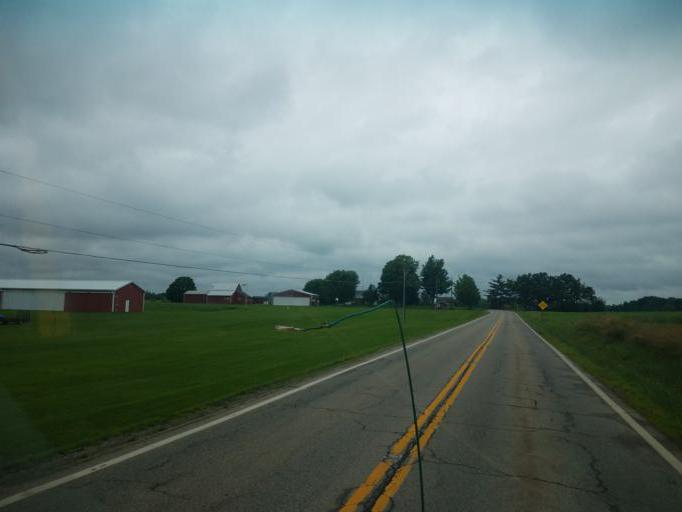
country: US
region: Ohio
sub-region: Carroll County
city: Carrollton
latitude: 40.6465
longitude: -81.0636
